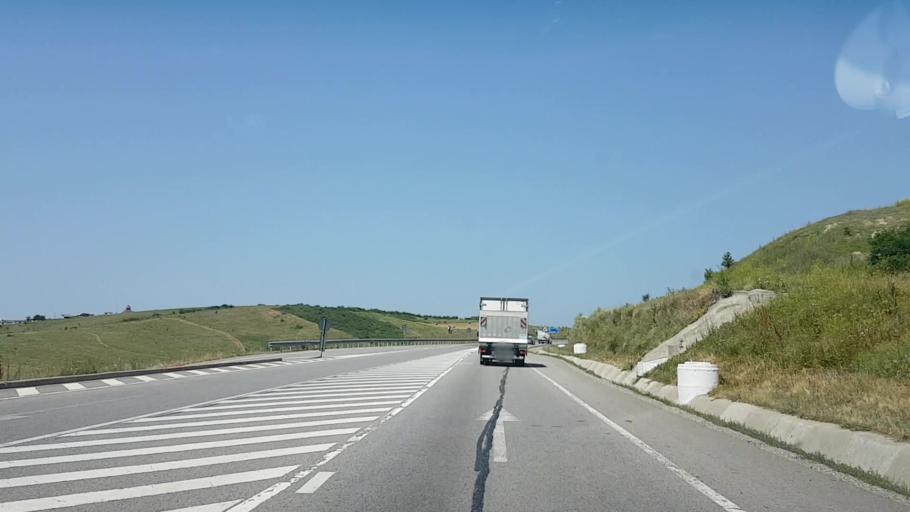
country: RO
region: Cluj
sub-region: Comuna Apahida
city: Dezmir
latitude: 46.7678
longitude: 23.6905
